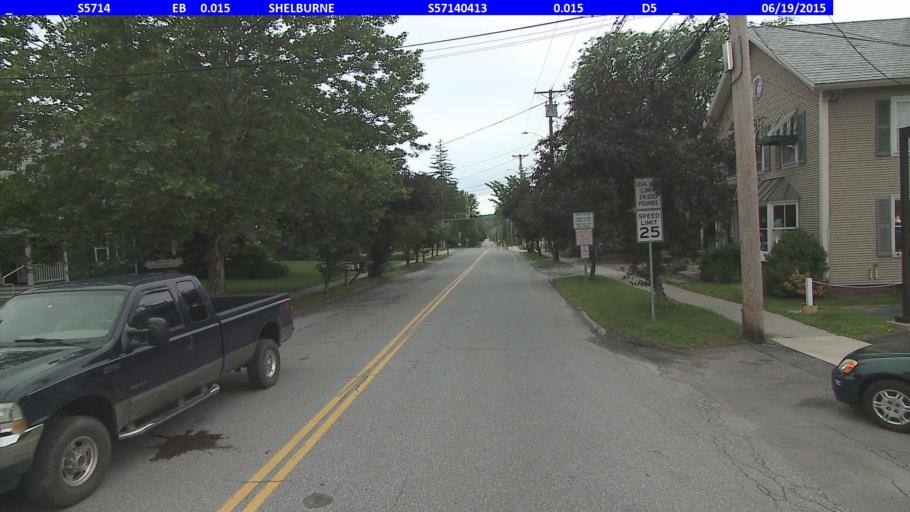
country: US
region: Vermont
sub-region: Chittenden County
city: Burlington
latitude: 44.3808
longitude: -73.2278
